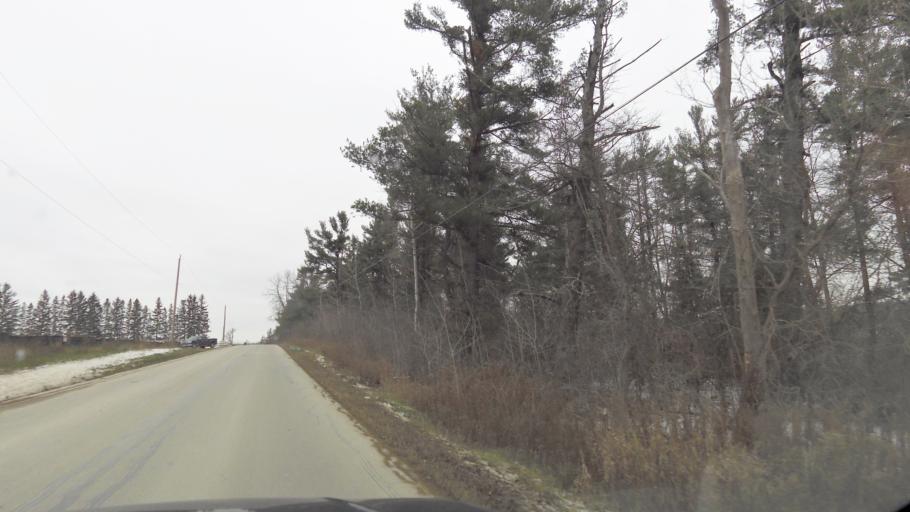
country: CA
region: Ontario
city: Vaughan
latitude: 43.8567
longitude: -79.6155
